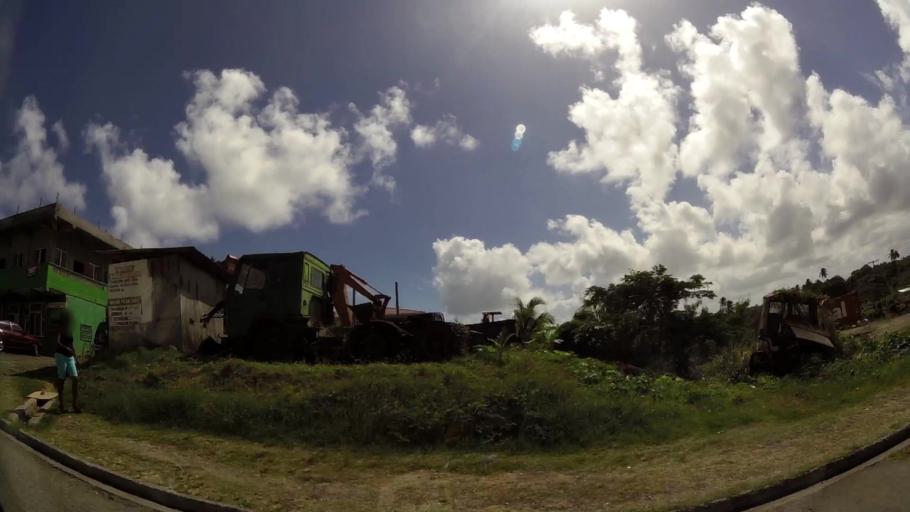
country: LC
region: Micoud Quarter
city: Micoud
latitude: 13.8176
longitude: -60.9006
